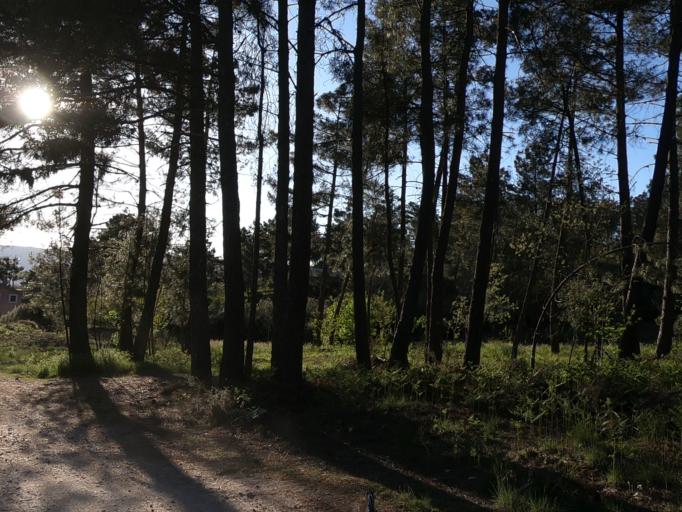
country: PT
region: Vila Real
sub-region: Sabrosa
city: Sabrosa
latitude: 41.3529
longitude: -7.6411
